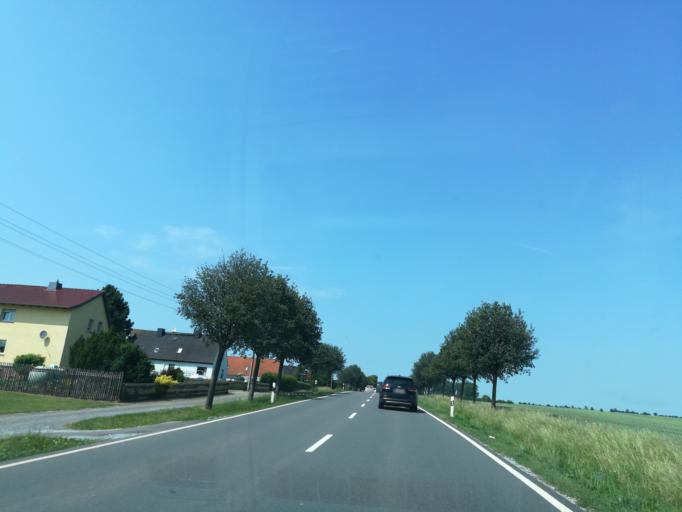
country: DE
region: Saxony-Anhalt
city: Aschersleben
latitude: 51.8197
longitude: 11.4568
